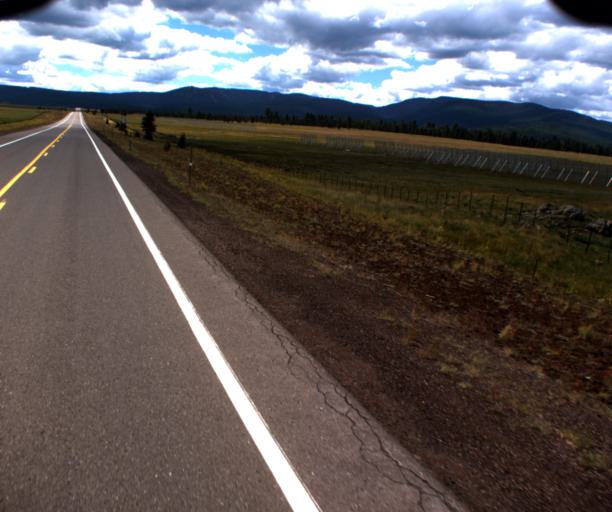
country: US
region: Arizona
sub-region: Apache County
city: Eagar
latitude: 34.0406
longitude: -109.5905
